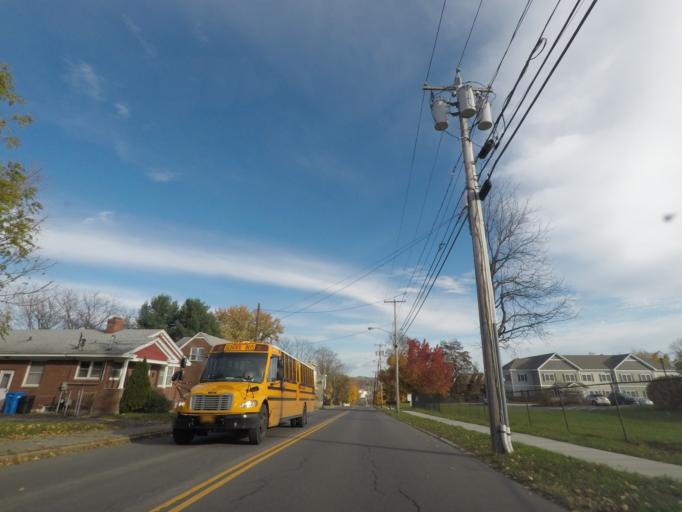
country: US
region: New York
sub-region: Albany County
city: Albany
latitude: 42.6345
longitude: -73.7691
